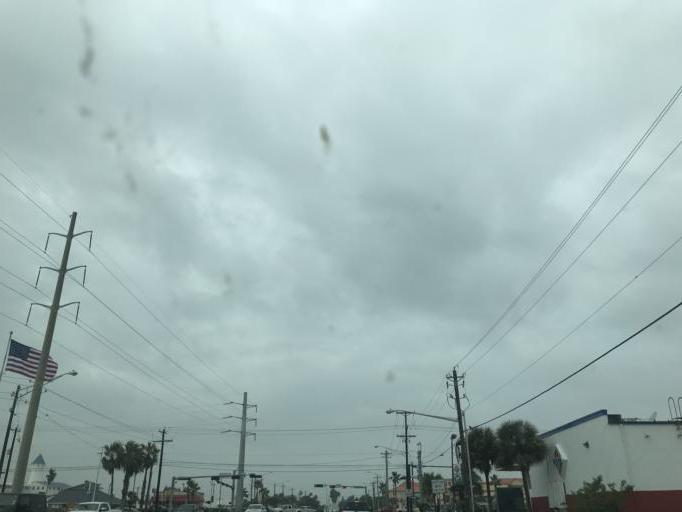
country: US
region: Texas
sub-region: Nueces County
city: Corpus Christi
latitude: 27.6181
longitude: -97.2206
